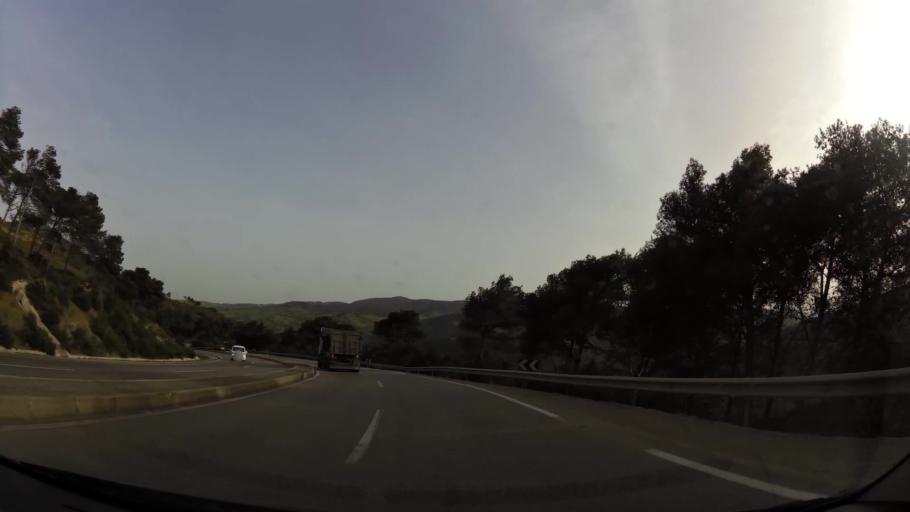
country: MA
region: Tanger-Tetouan
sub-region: Tetouan
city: Saddina
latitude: 35.5542
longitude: -5.5689
